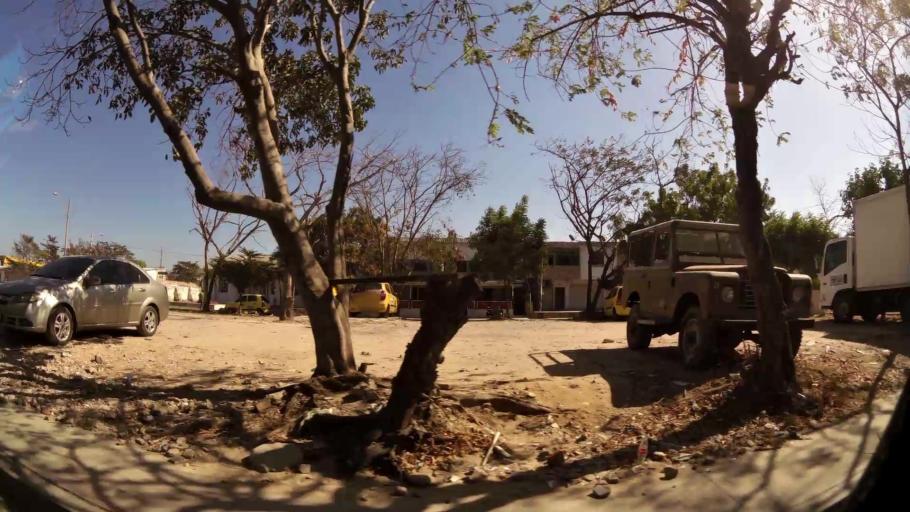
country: CO
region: Atlantico
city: Soledad
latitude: 10.9315
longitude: -74.7853
